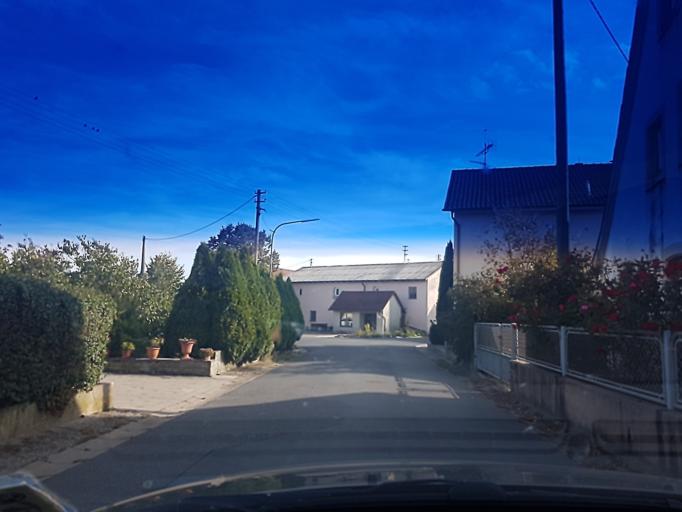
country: DE
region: Bavaria
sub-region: Regierungsbezirk Mittelfranken
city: Burghaslach
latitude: 49.7760
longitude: 10.5447
